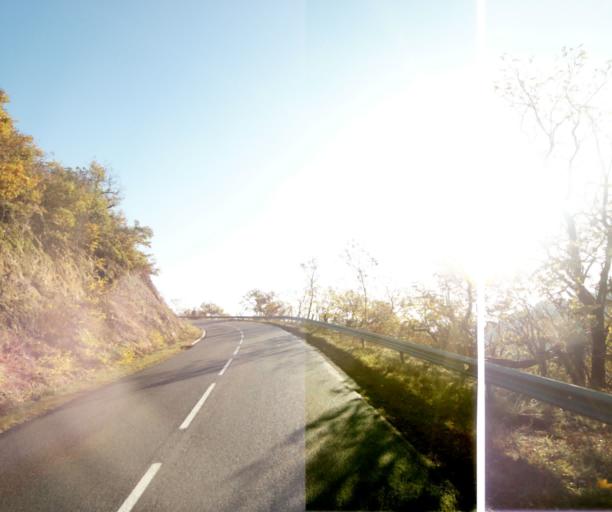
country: FR
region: Auvergne
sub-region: Departement du Puy-de-Dome
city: Nohanent
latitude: 45.8080
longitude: 3.0435
